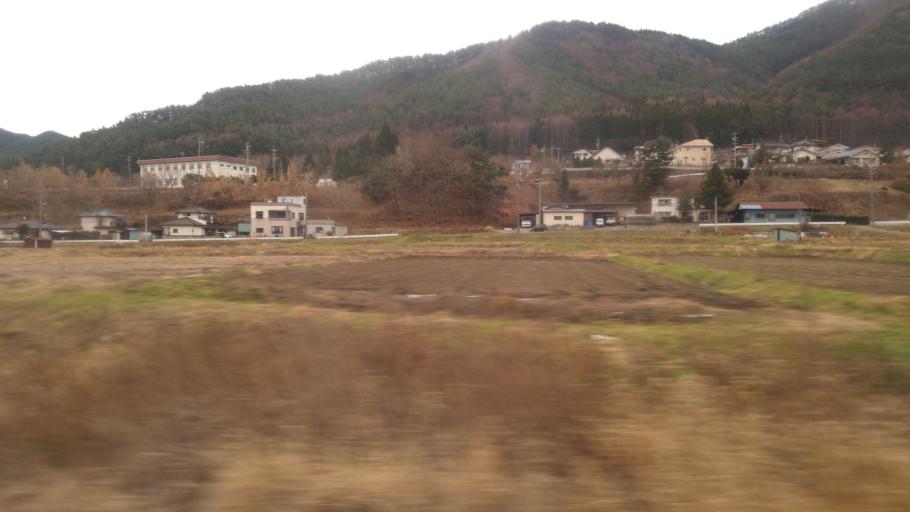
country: JP
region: Nagano
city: Shiojiri
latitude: 36.0776
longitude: 137.9079
